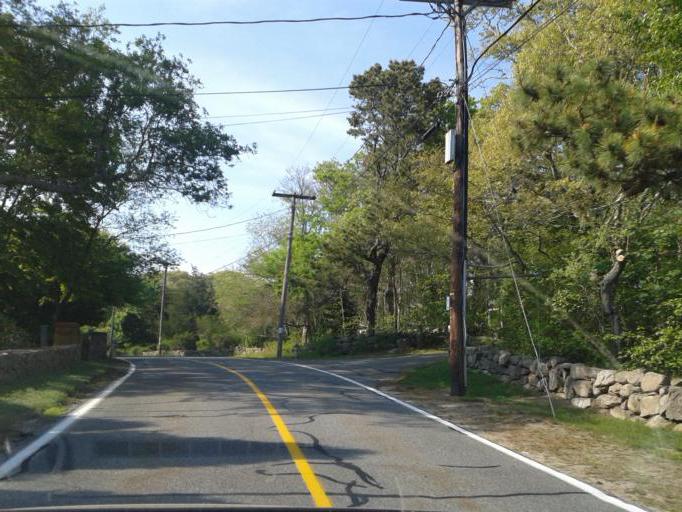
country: US
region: Massachusetts
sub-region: Barnstable County
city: Falmouth
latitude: 41.5194
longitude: -70.6617
